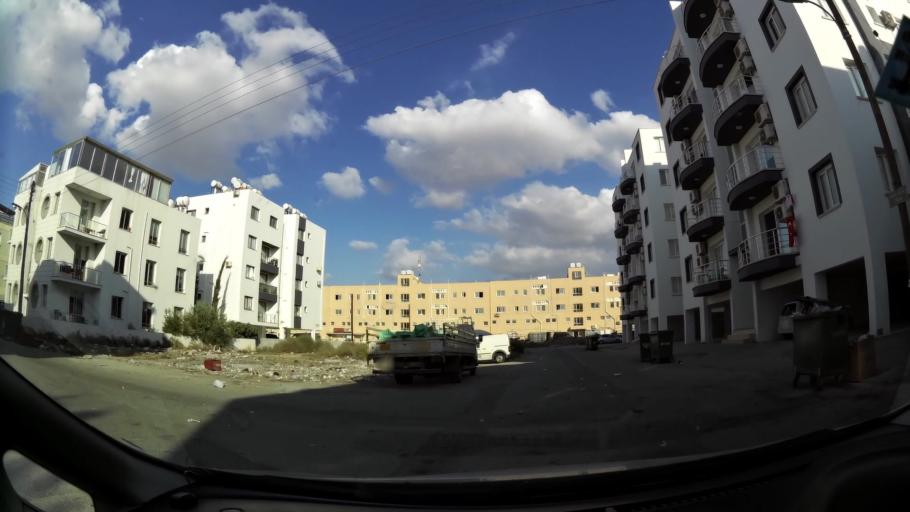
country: CY
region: Lefkosia
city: Nicosia
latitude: 35.1962
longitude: 33.3666
